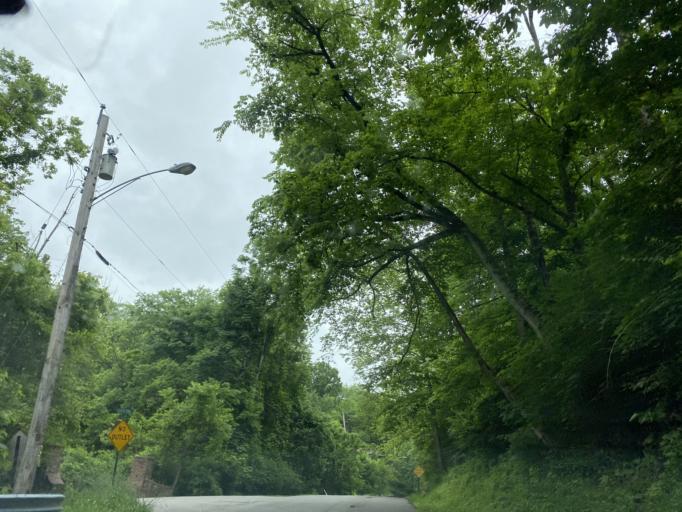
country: US
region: Kentucky
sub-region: Campbell County
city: Dayton
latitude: 39.1023
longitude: -84.4581
